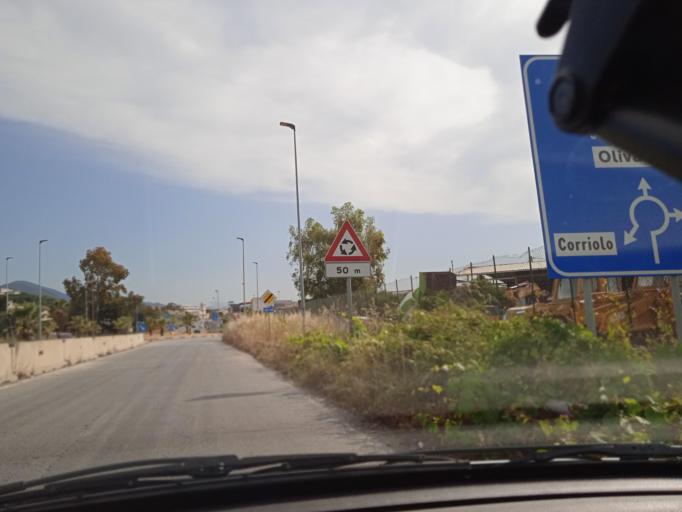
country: IT
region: Sicily
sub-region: Messina
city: San Filippo del Mela
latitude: 38.1847
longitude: 15.2702
